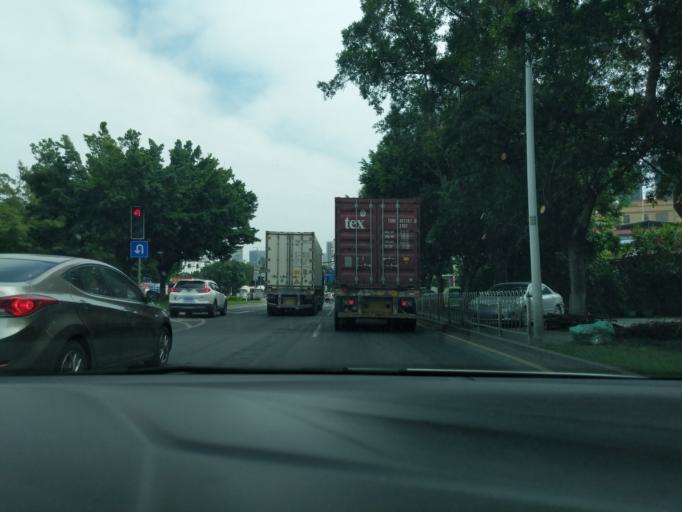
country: CN
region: Guangdong
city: Nansha
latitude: 22.7524
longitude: 113.5772
